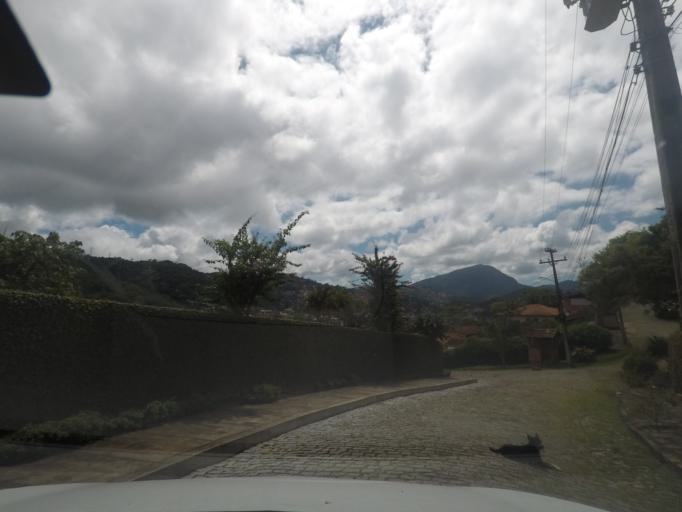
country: BR
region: Rio de Janeiro
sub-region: Teresopolis
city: Teresopolis
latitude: -22.3989
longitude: -42.9856
